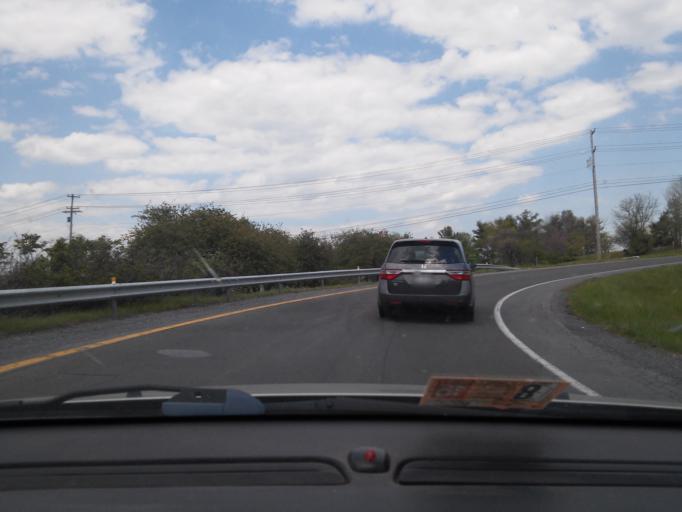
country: US
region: Virginia
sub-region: City of Winchester
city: Winchester
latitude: 39.1624
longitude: -78.1595
